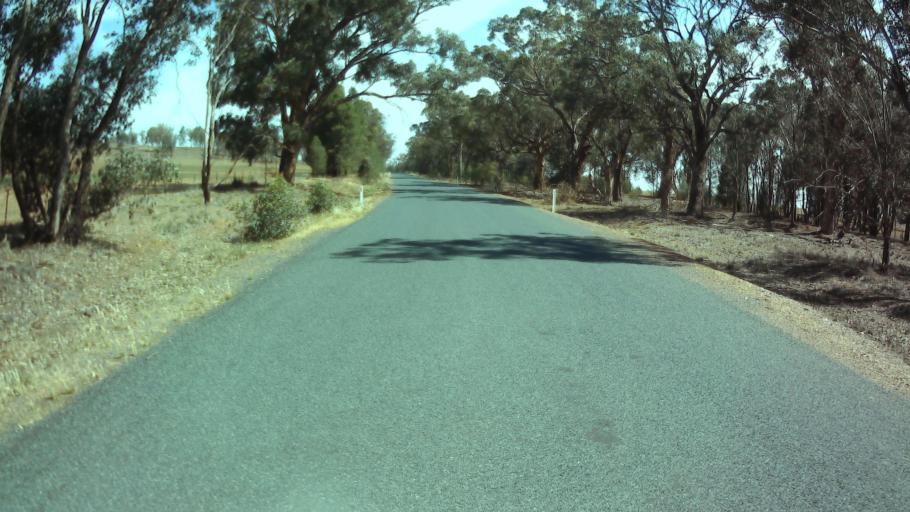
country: AU
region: New South Wales
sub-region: Weddin
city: Grenfell
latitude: -34.0479
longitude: 148.1309
